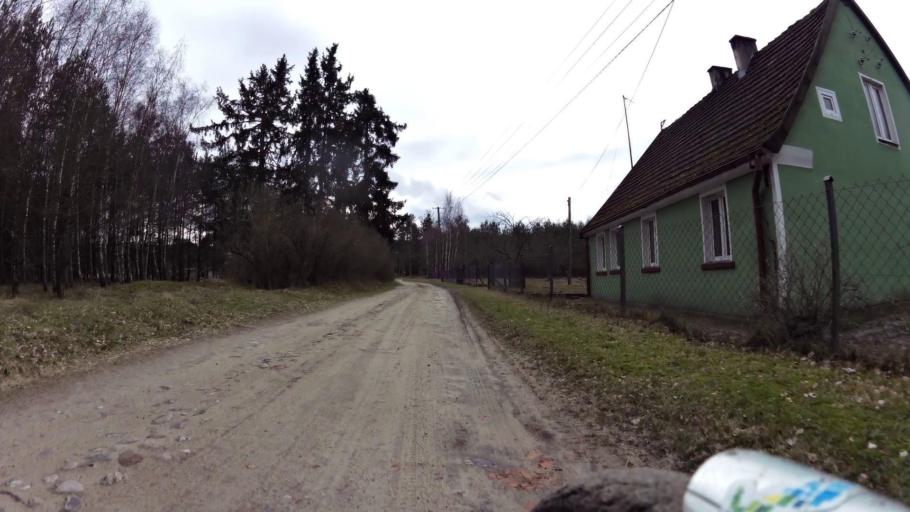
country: PL
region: Pomeranian Voivodeship
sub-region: Powiat bytowski
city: Kolczyglowy
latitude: 54.1547
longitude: 17.1869
